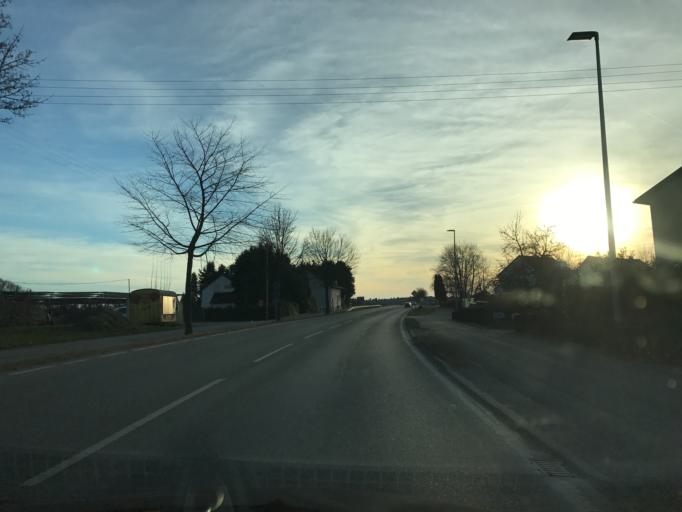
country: DE
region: Baden-Wuerttemberg
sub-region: Tuebingen Region
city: Meckenbeuren
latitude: 47.6789
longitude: 9.5480
